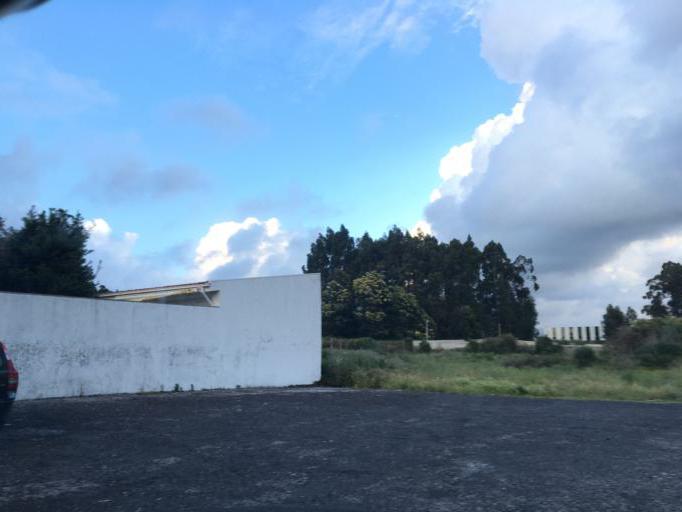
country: PT
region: Porto
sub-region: Maia
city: Anta
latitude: 41.2489
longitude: -8.6358
